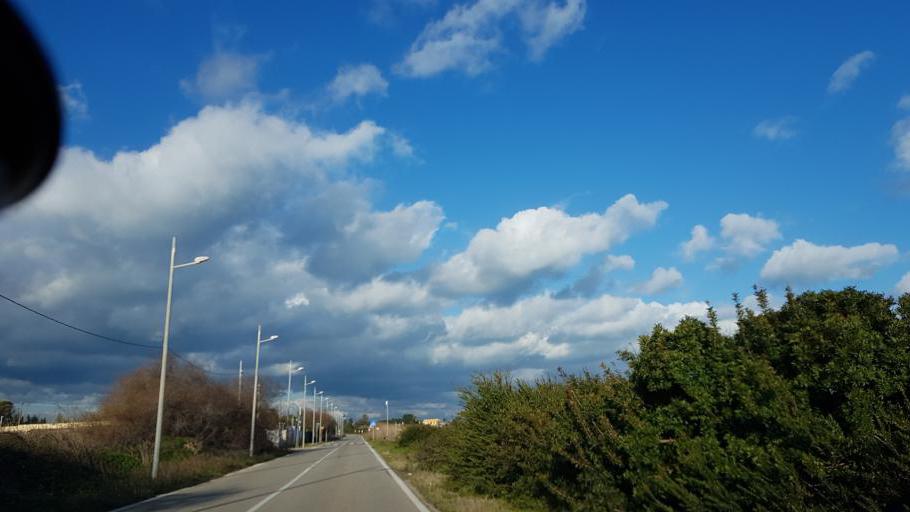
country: IT
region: Apulia
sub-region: Provincia di Brindisi
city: Materdomini
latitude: 40.6765
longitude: 17.9430
